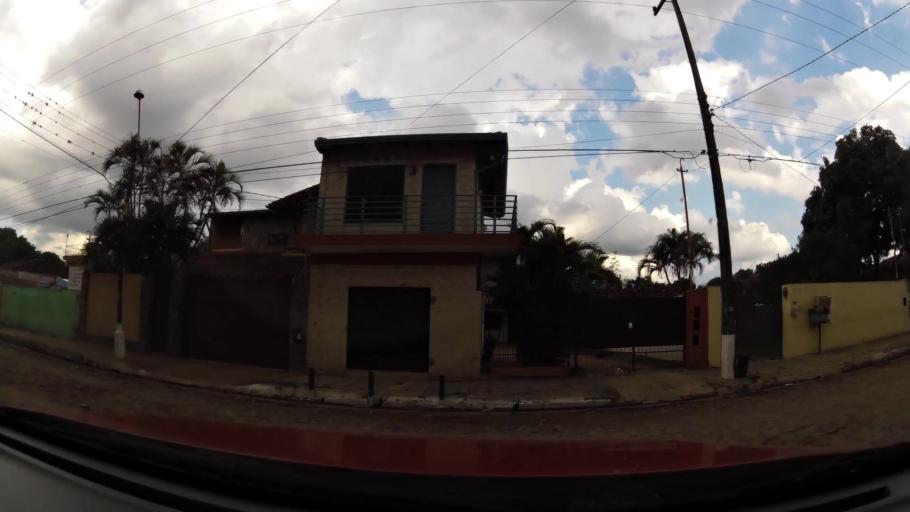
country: PY
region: Central
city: Fernando de la Mora
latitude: -25.3382
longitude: -57.5508
